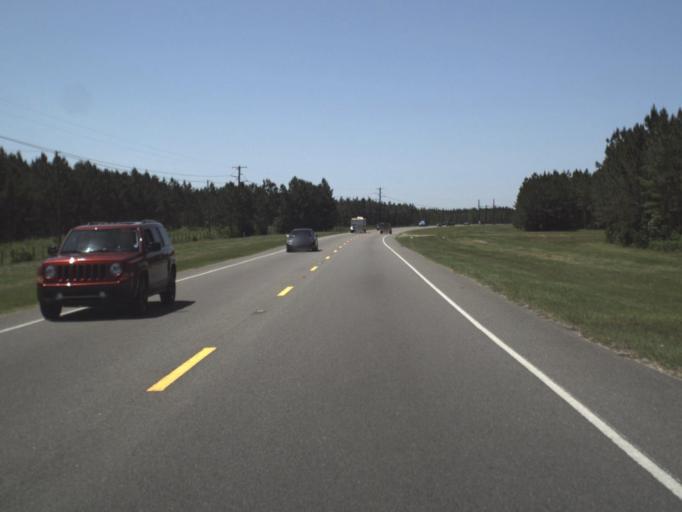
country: US
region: Florida
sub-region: Clay County
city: Lakeside
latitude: 30.1817
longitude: -81.8351
